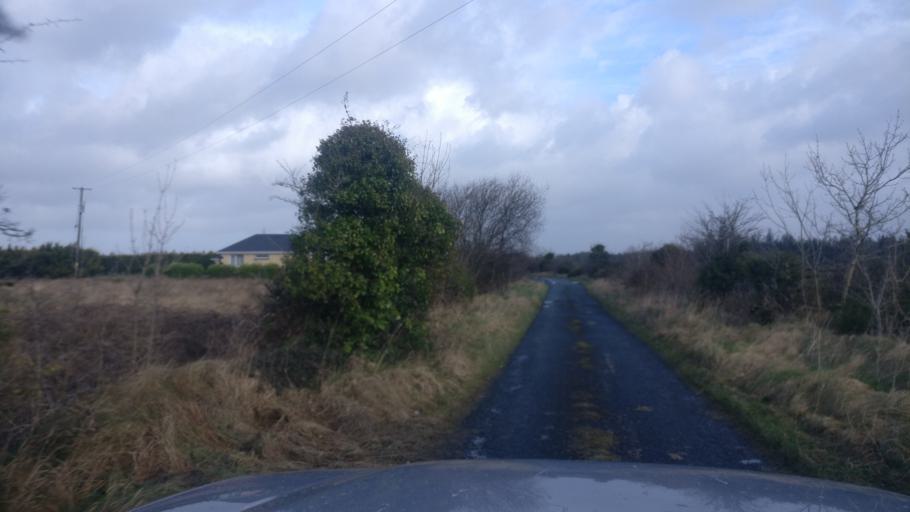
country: IE
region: Connaught
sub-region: County Galway
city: Loughrea
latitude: 53.2311
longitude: -8.5359
